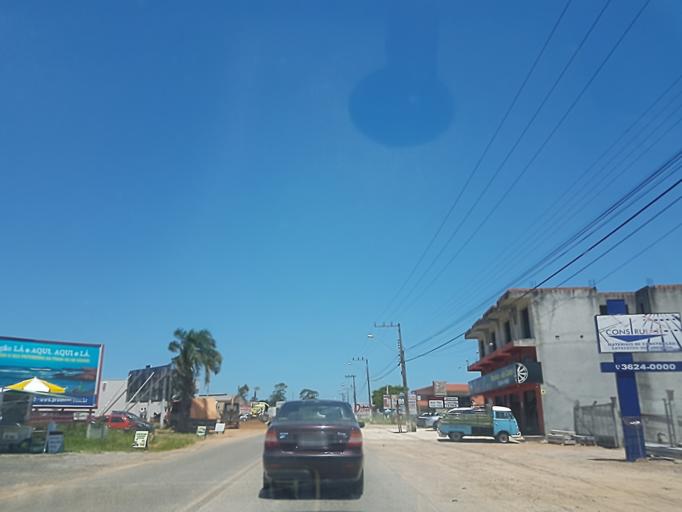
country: BR
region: Santa Catarina
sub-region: Jaguaruna
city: Jaguaruna
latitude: -28.6052
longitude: -49.0340
